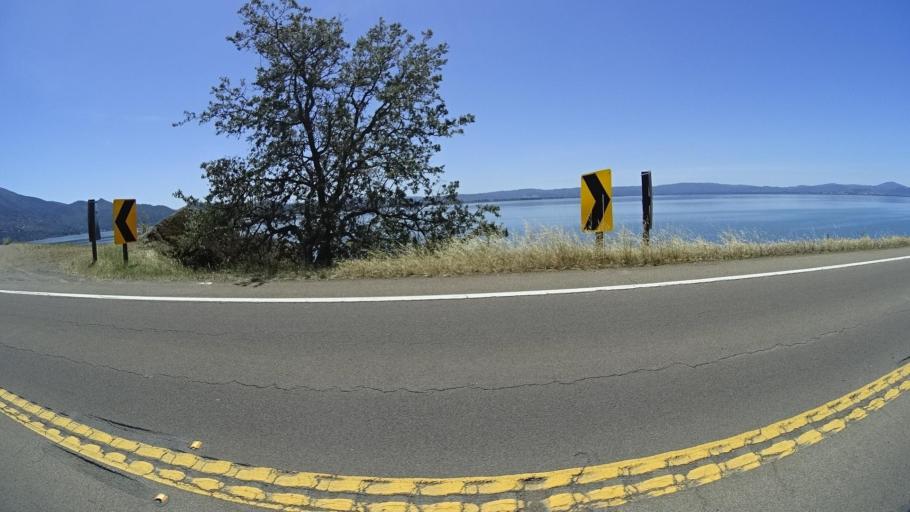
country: US
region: California
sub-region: Lake County
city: Soda Bay
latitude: 39.0445
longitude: -122.7782
